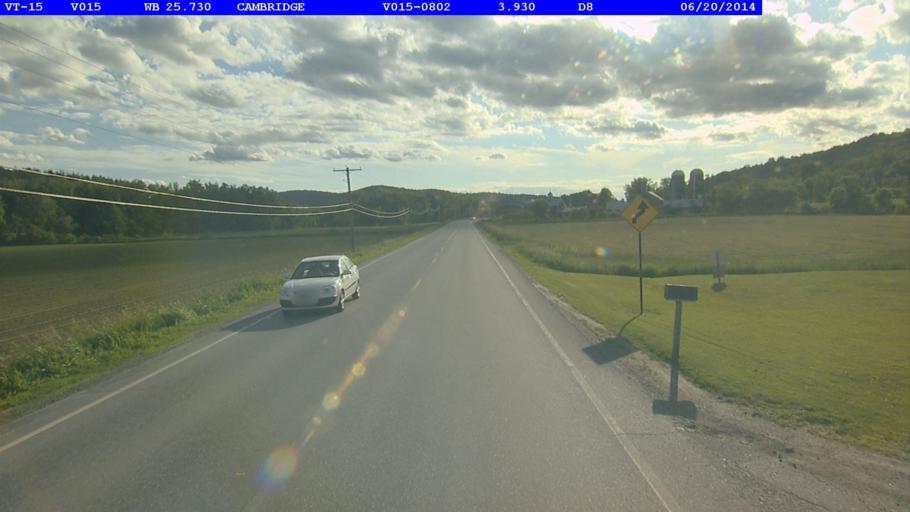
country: US
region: Vermont
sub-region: Lamoille County
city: Johnson
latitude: 44.6454
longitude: -72.8512
